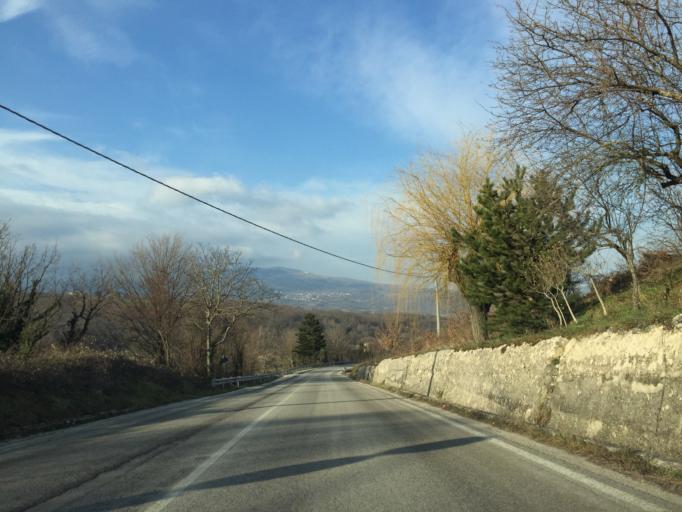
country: IT
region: Molise
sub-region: Provincia di Campobasso
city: San Massimo
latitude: 41.4923
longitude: 14.4088
